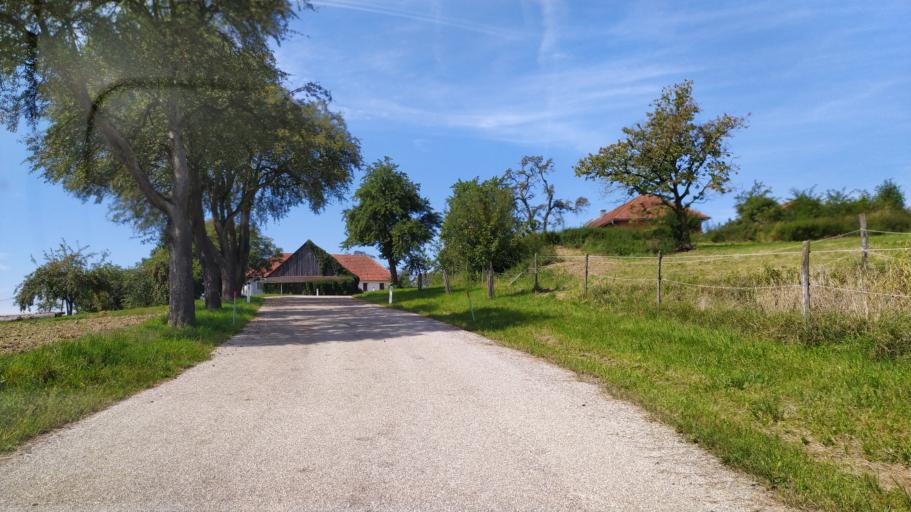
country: AT
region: Lower Austria
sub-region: Politischer Bezirk Amstetten
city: Strengberg
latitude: 48.1387
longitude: 14.6129
